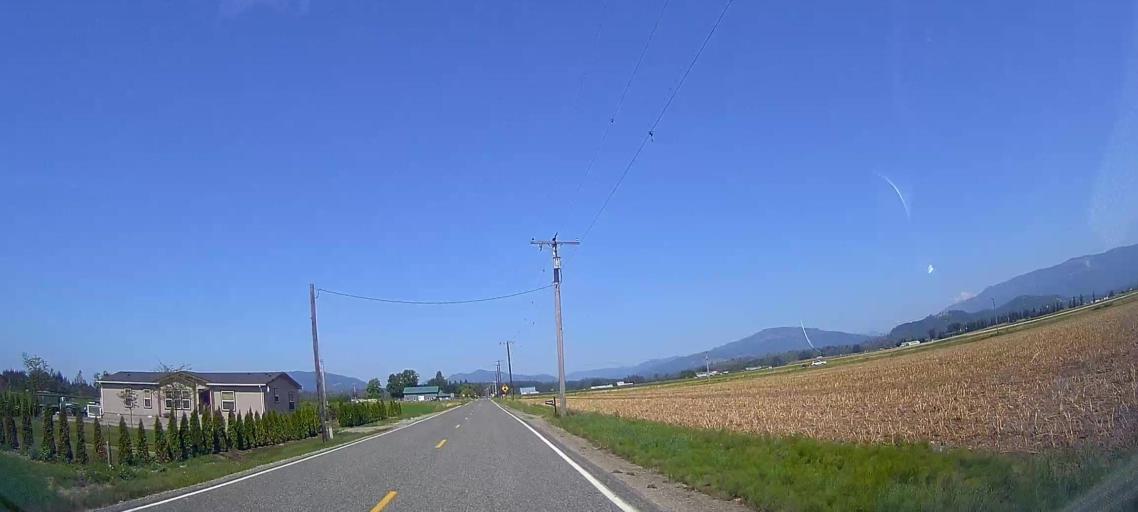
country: US
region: Washington
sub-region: Skagit County
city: Burlington
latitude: 48.4975
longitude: -122.3571
